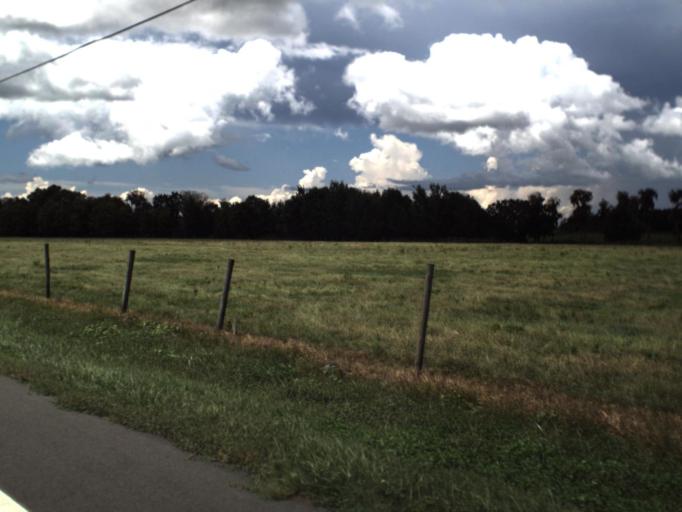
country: US
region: Florida
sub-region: Polk County
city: Crooked Lake Park
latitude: 27.7334
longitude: -81.6568
